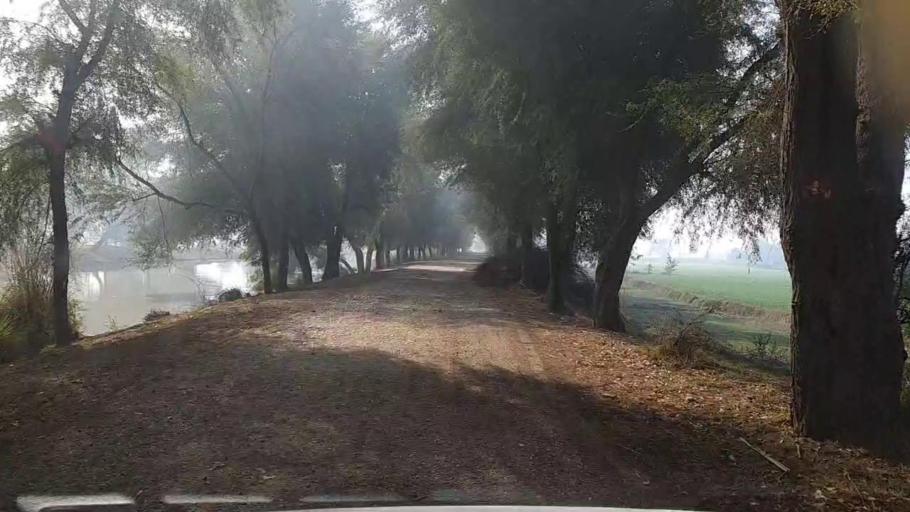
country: PK
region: Sindh
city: Khairpur
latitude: 27.9547
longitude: 69.6531
